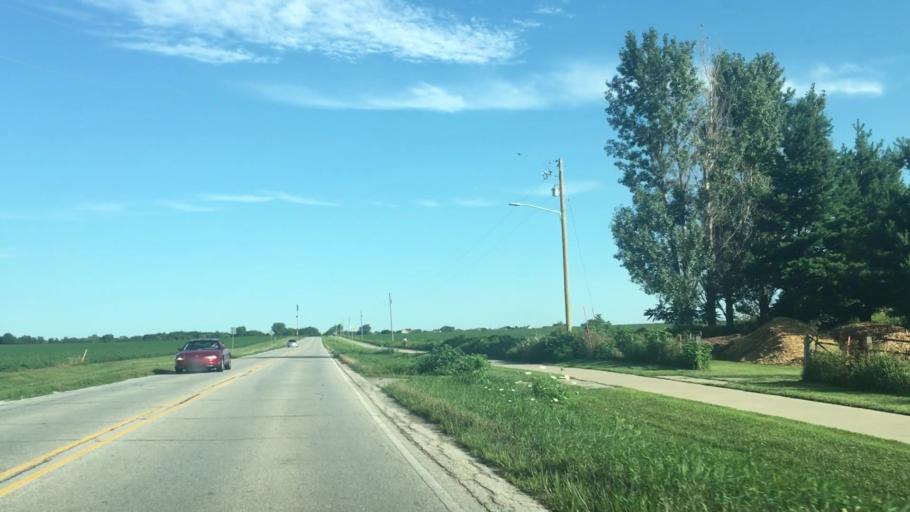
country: US
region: Iowa
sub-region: Johnson County
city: North Liberty
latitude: 41.7343
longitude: -91.5804
